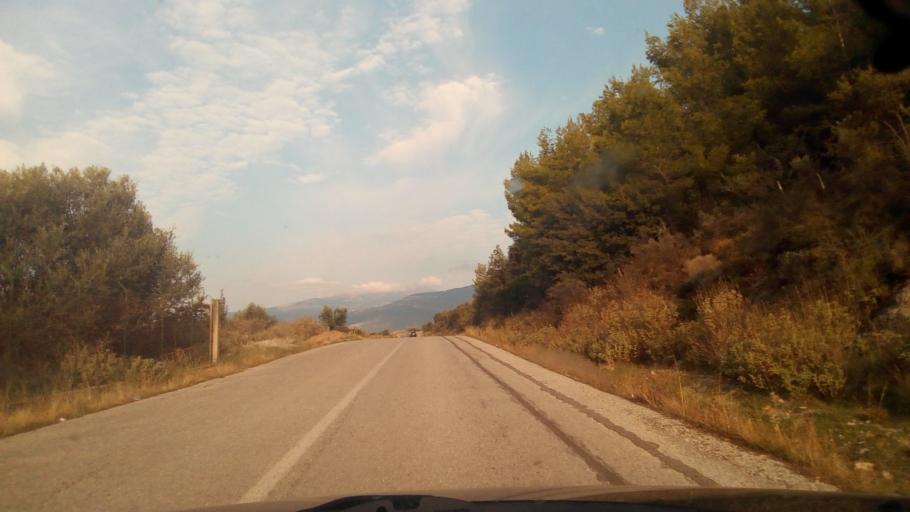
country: GR
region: West Greece
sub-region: Nomos Aitolias kai Akarnanias
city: Nafpaktos
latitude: 38.4089
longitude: 21.9325
